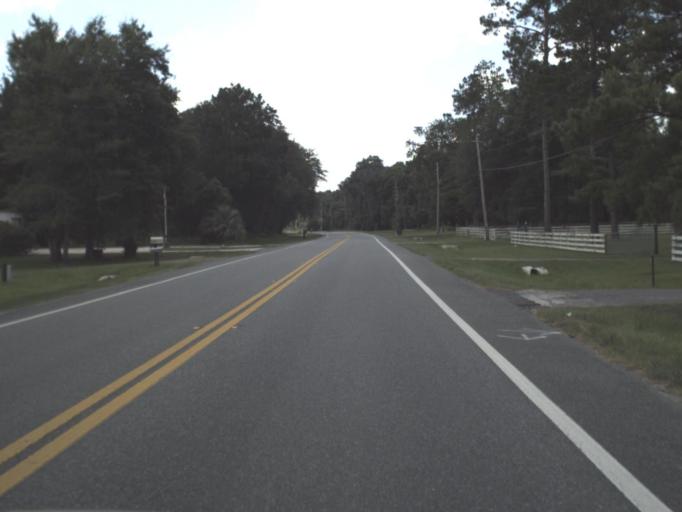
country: US
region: Florida
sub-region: Baker County
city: Macclenny
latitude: 30.3379
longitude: -82.1252
